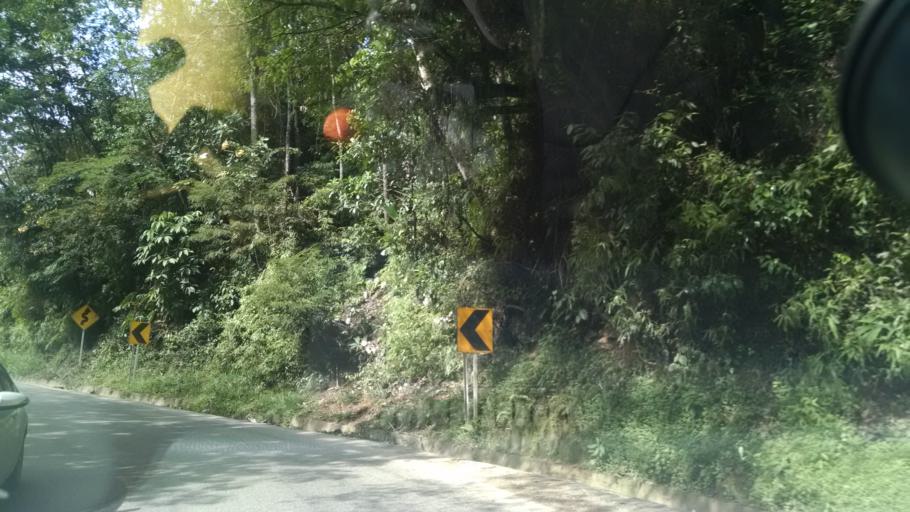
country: CO
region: Antioquia
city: Santo Domingo
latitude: 6.5453
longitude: -75.2217
